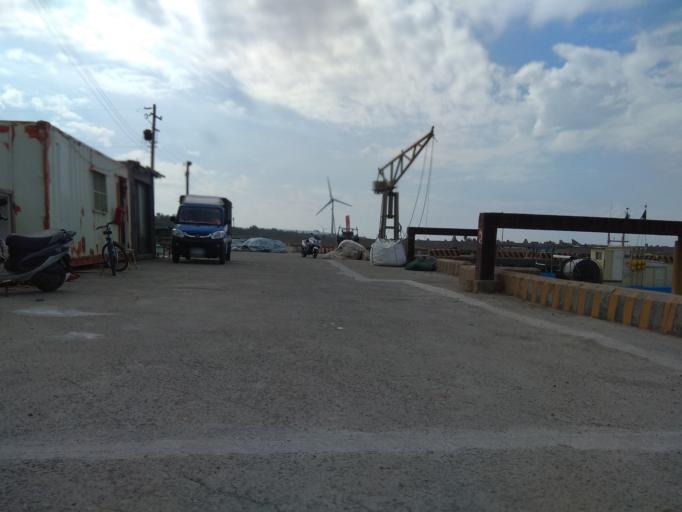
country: TW
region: Taiwan
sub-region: Hsinchu
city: Zhubei
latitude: 24.9272
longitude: 120.9724
